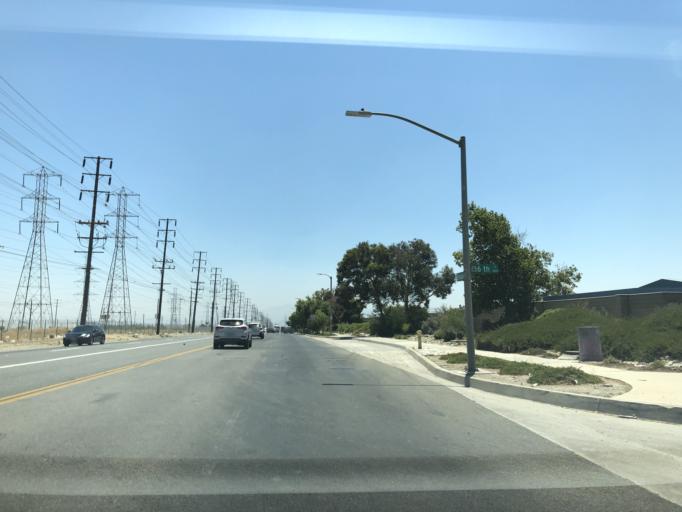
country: US
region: California
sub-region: San Bernardino County
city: Rancho Cucamonga
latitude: 34.0864
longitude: -117.5239
